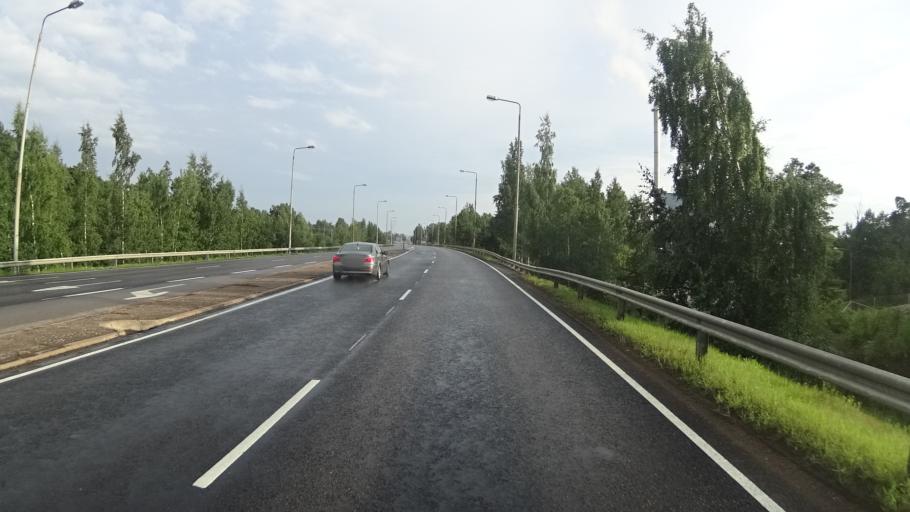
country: FI
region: Kymenlaakso
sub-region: Kotka-Hamina
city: Kotka
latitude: 60.4731
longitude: 26.9177
